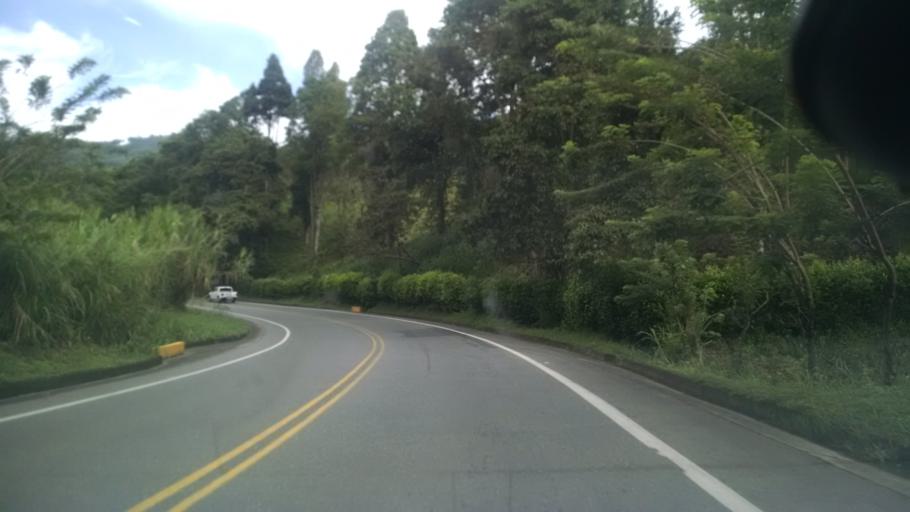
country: CO
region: Caldas
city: Palestina
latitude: 5.0676
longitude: -75.6190
